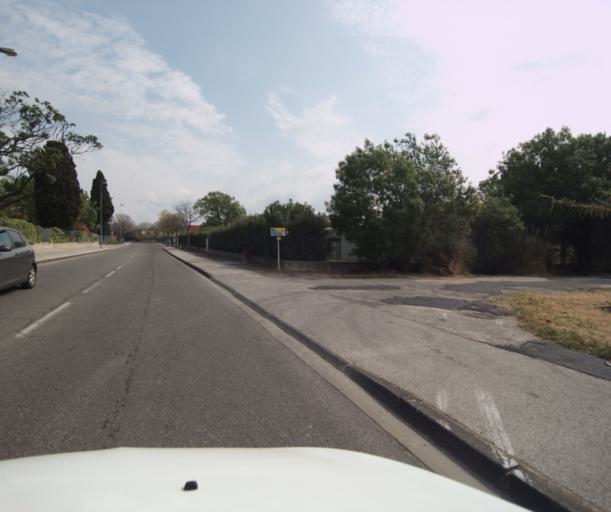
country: FR
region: Provence-Alpes-Cote d'Azur
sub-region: Departement du Var
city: La Garde
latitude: 43.1314
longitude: 6.0252
